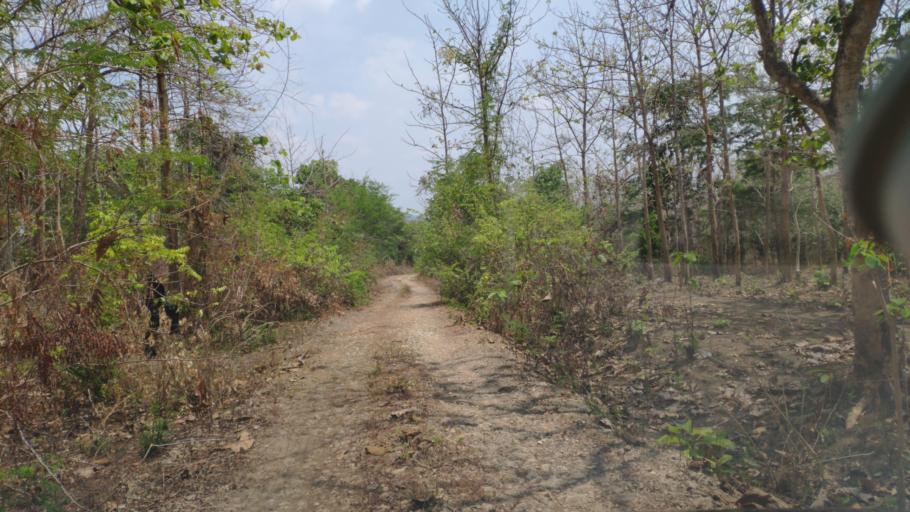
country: ID
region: Central Java
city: Padaan
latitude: -6.9299
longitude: 111.3054
